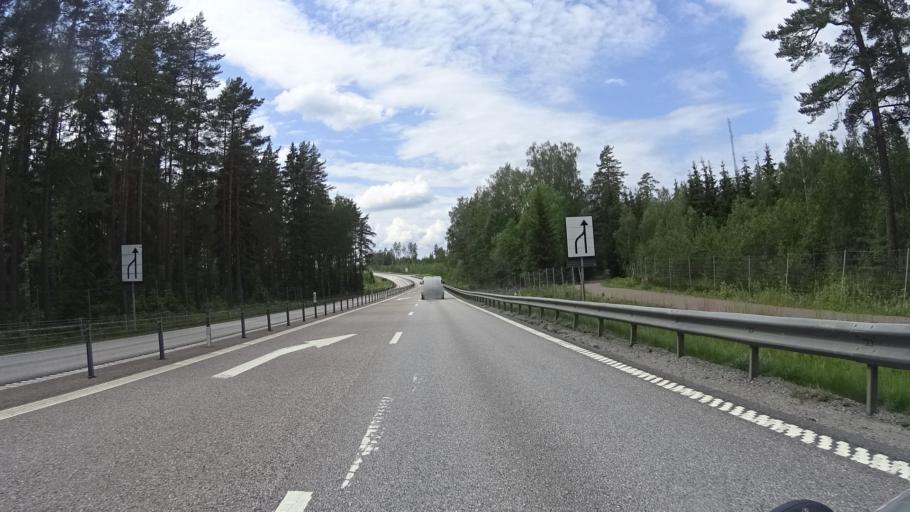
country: SE
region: OErebro
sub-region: Laxa Kommun
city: Laxa
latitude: 58.9761
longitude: 14.5713
